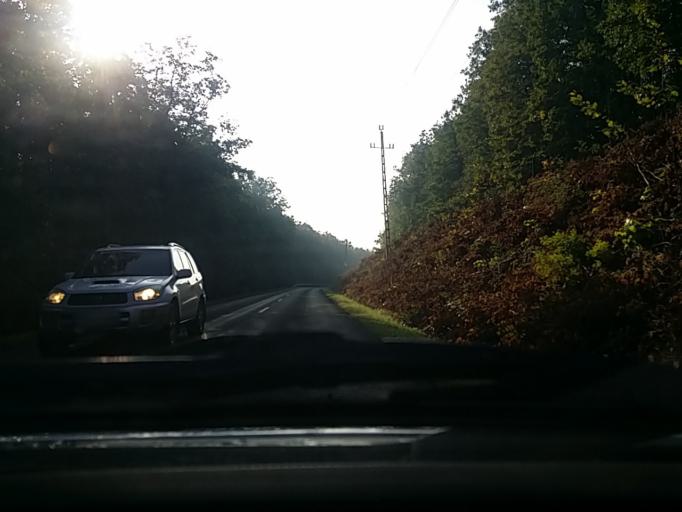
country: HU
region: Pest
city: Nagykovacsi
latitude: 47.7175
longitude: 19.0098
